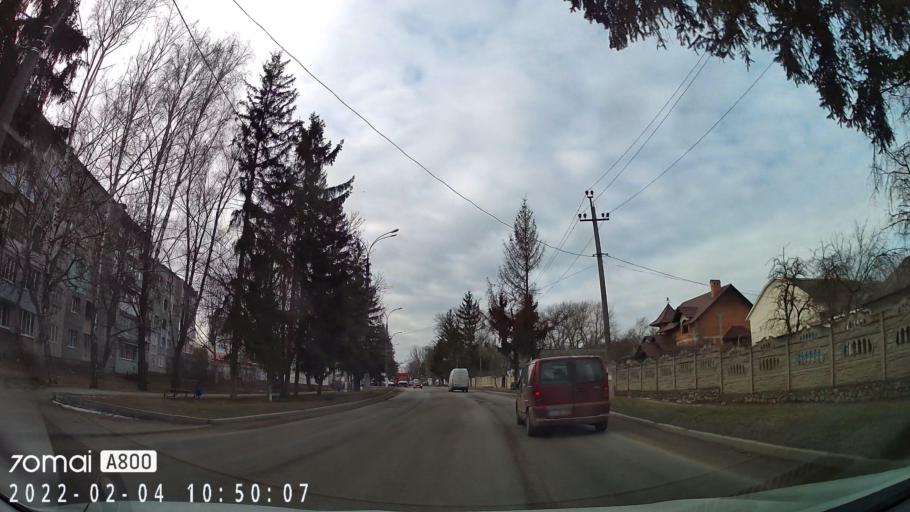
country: MD
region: Briceni
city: Briceni
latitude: 48.3555
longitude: 27.0875
